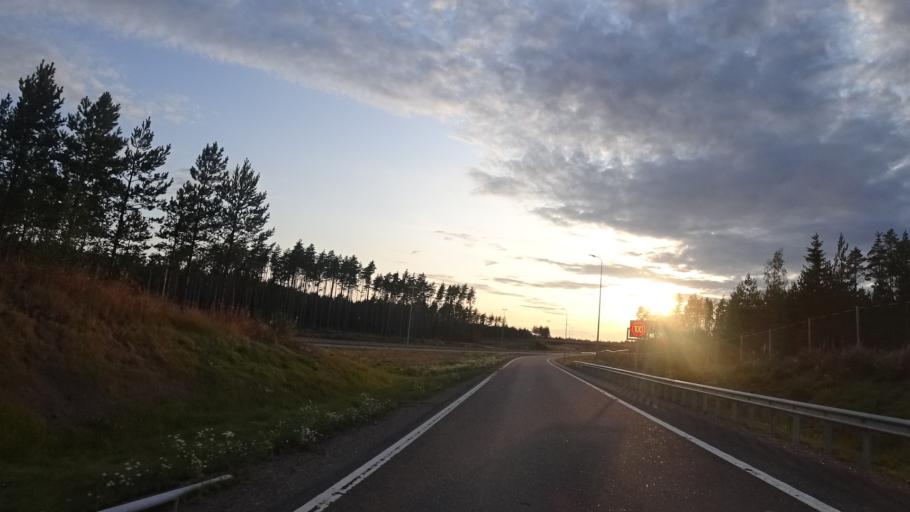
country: FI
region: Kymenlaakso
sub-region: Kotka-Hamina
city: Virojoki
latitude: 60.6114
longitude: 27.8138
